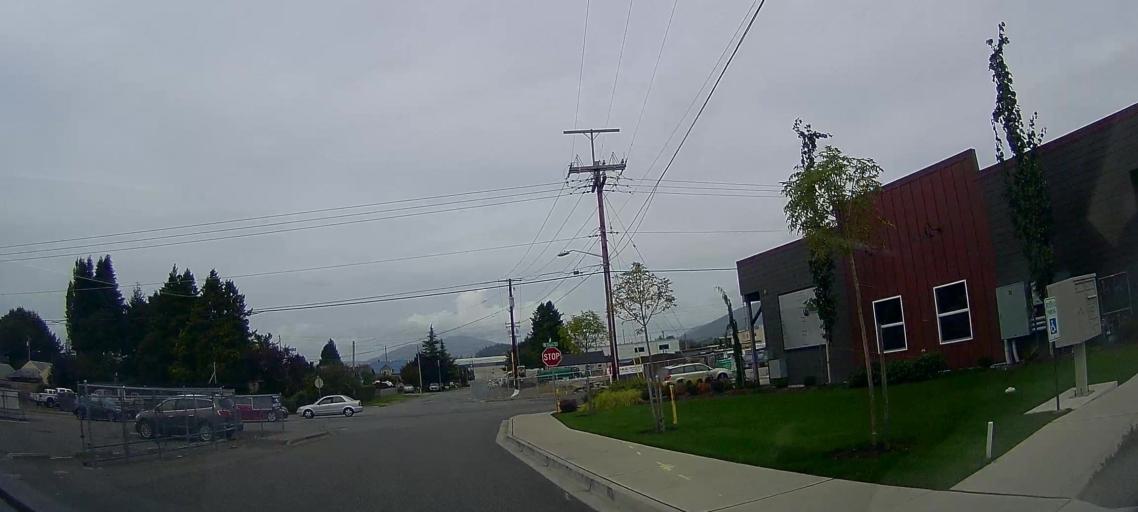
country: US
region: Washington
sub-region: Skagit County
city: Sedro-Woolley
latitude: 48.5027
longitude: -122.2420
